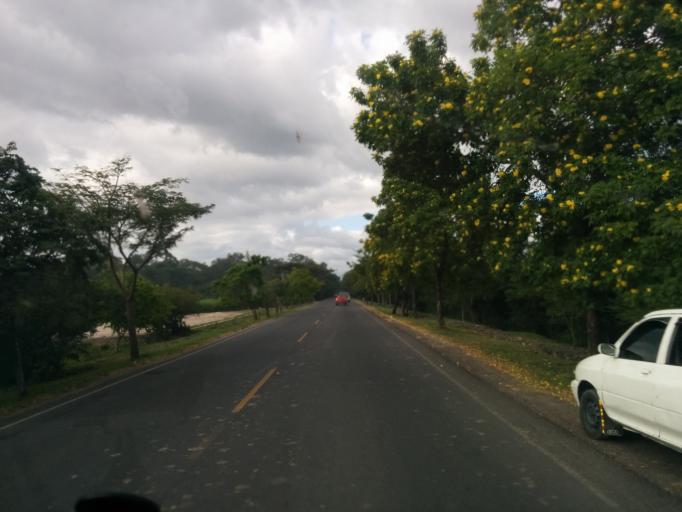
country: NI
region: Esteli
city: Esteli
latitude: 13.1318
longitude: -86.3652
